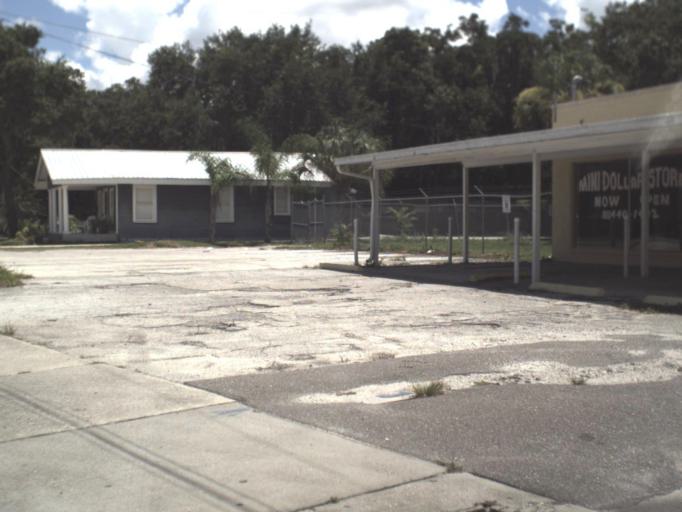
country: US
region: Florida
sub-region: Hillsborough County
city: Plant City
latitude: 28.0152
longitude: -82.1357
